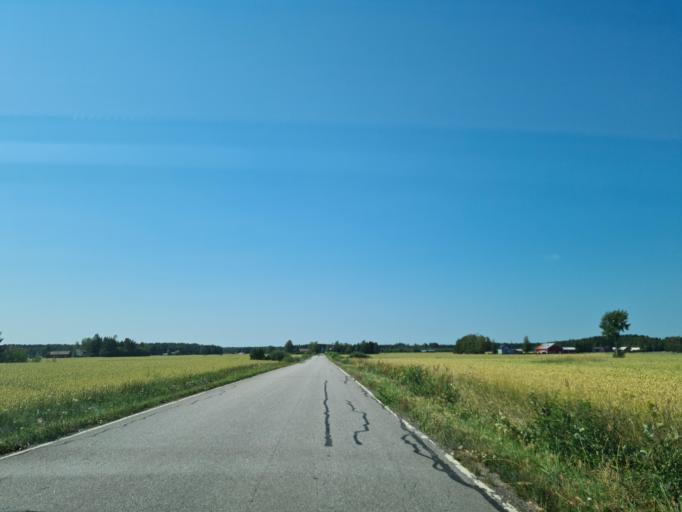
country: FI
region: Varsinais-Suomi
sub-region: Loimaa
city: Aura
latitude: 60.6026
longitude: 22.6480
